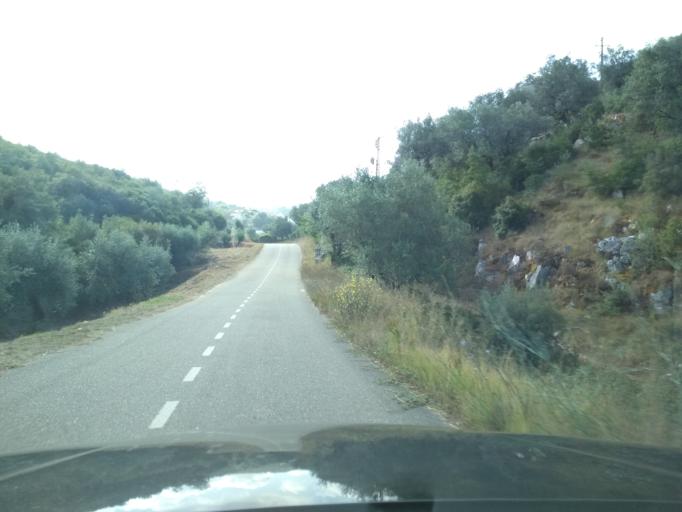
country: PT
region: Coimbra
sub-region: Condeixa-A-Nova
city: Condeixa-a-Nova
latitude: 40.0721
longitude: -8.5012
